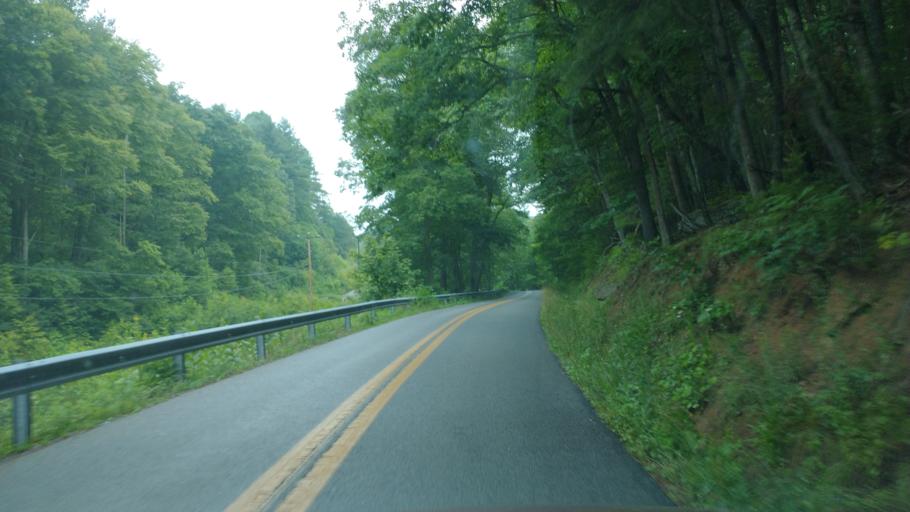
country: US
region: West Virginia
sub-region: Mercer County
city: Athens
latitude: 37.4344
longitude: -80.9677
